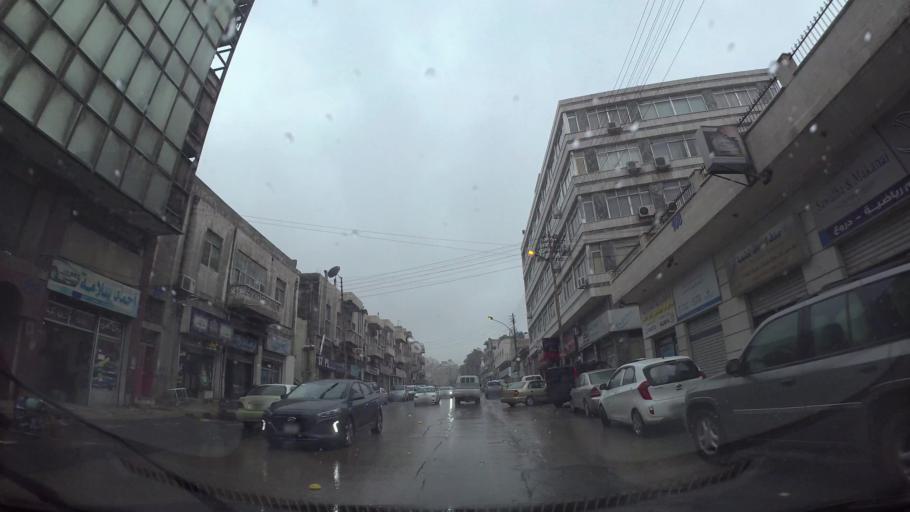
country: JO
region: Amman
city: Amman
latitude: 31.9588
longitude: 35.9273
